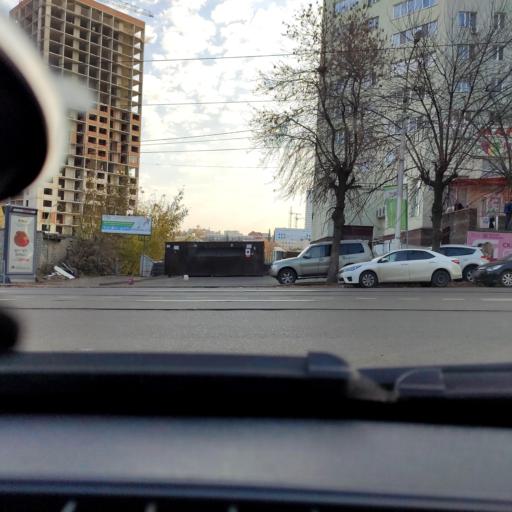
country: RU
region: Bashkortostan
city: Ufa
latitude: 54.7476
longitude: 55.9596
